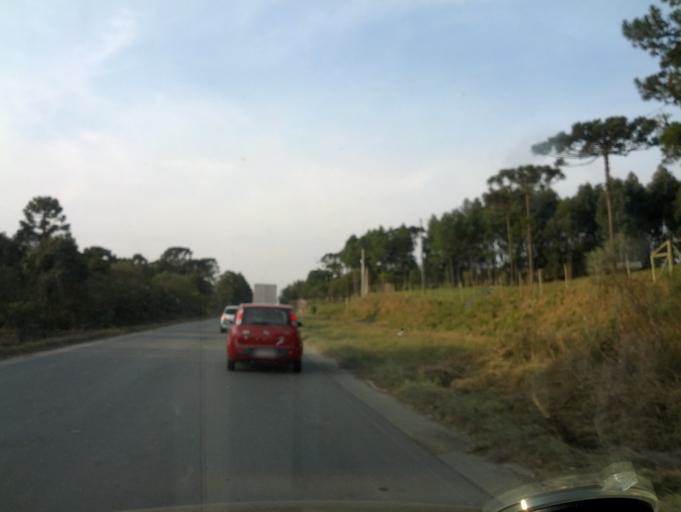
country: BR
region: Santa Catarina
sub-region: Otacilio Costa
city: Otacilio Costa
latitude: -27.5327
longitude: -50.1421
